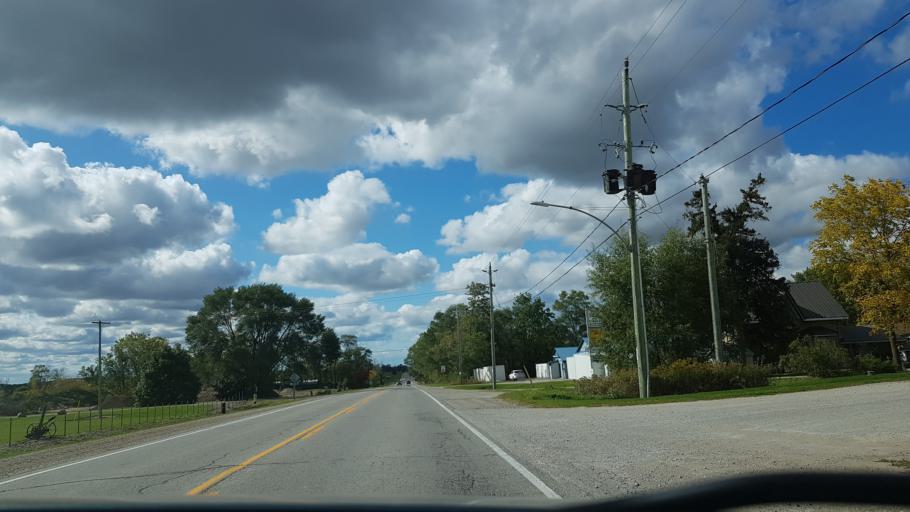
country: CA
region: Ontario
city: South Huron
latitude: 43.3608
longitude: -81.4931
